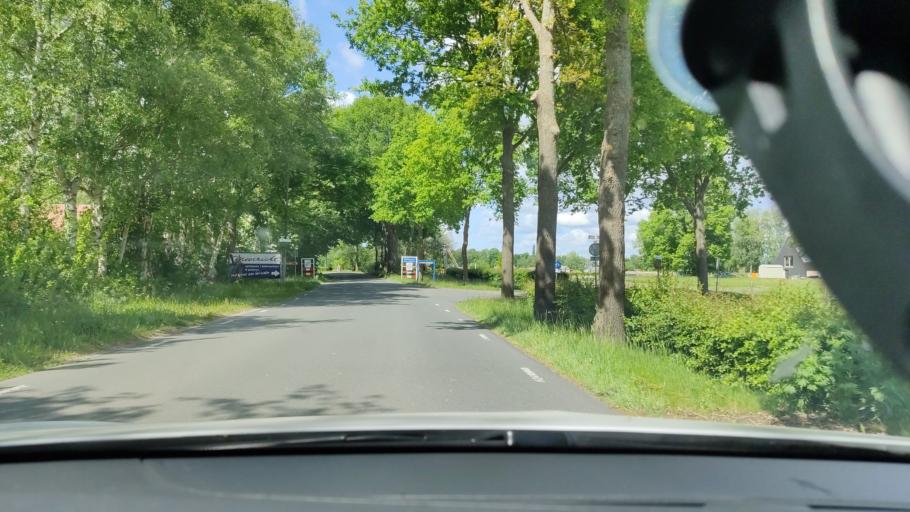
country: NL
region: Drenthe
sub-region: Gemeente Tynaarlo
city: Zuidlaren
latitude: 53.1072
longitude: 6.6837
